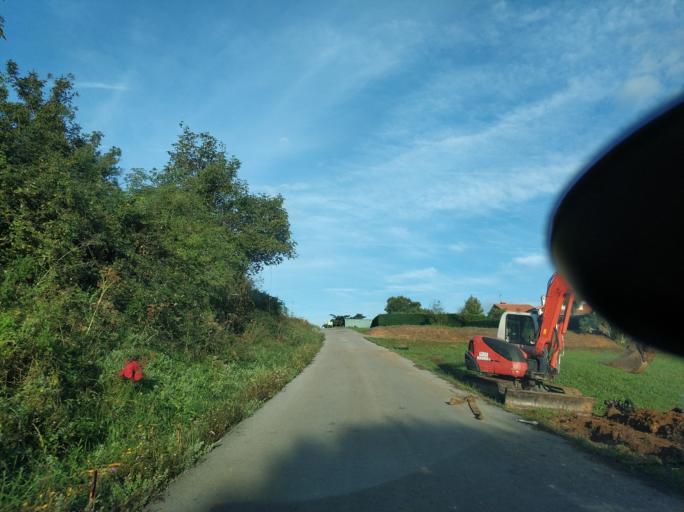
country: ES
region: Cantabria
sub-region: Provincia de Cantabria
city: Miengo
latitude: 43.4067
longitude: -3.9580
